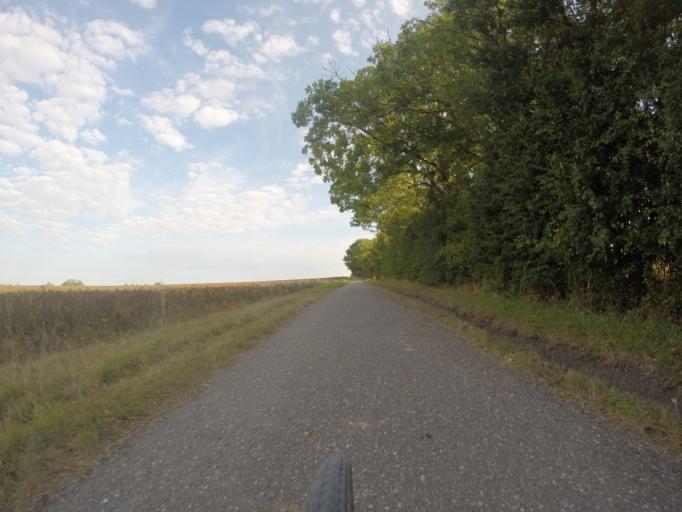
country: DK
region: Capital Region
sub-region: Egedal Kommune
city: Smorumnedre
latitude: 55.6964
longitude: 12.3145
